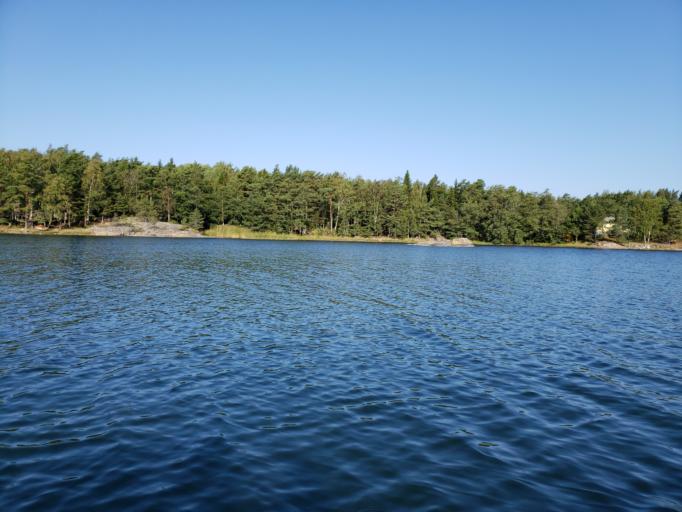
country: FI
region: Varsinais-Suomi
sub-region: Aboland-Turunmaa
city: Dragsfjaerd
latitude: 59.9118
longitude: 22.3777
